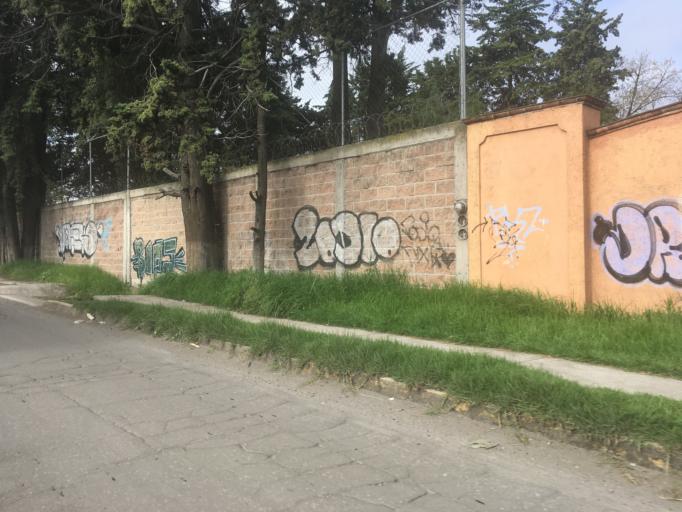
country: MX
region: Mexico
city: Santa Maria Totoltepec
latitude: 19.3002
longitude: -99.5940
